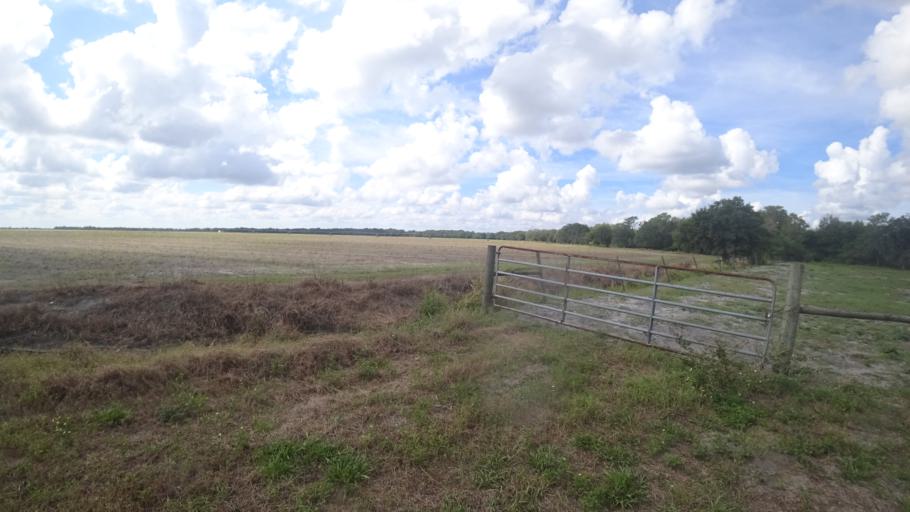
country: US
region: Florida
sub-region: Hillsborough County
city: Wimauma
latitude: 27.5923
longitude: -82.2722
